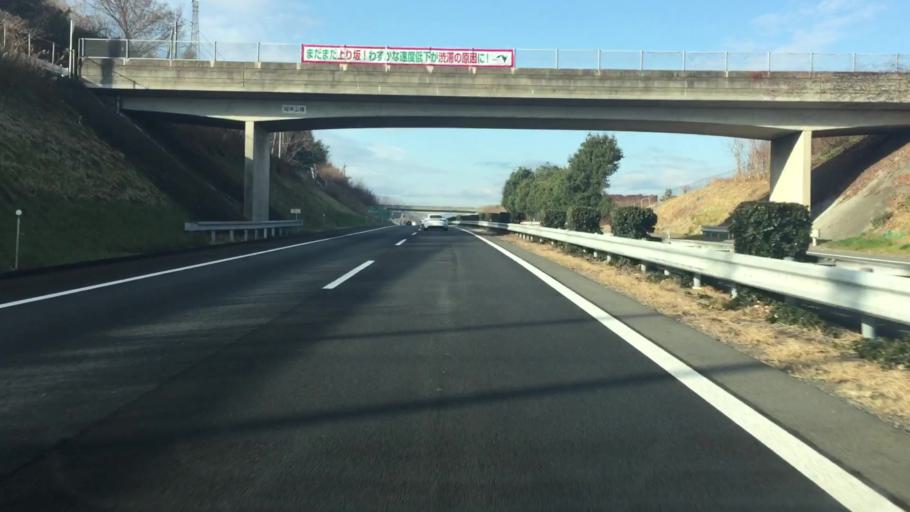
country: JP
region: Gunma
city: Yoshii
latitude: 36.2412
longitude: 138.9734
